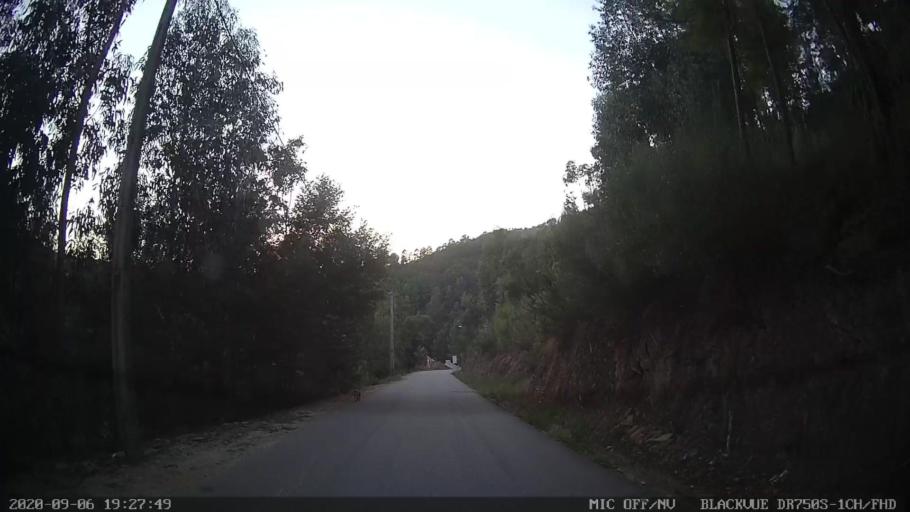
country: PT
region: Vila Real
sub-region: Mesao Frio
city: Mesao Frio
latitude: 41.1805
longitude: -7.9079
